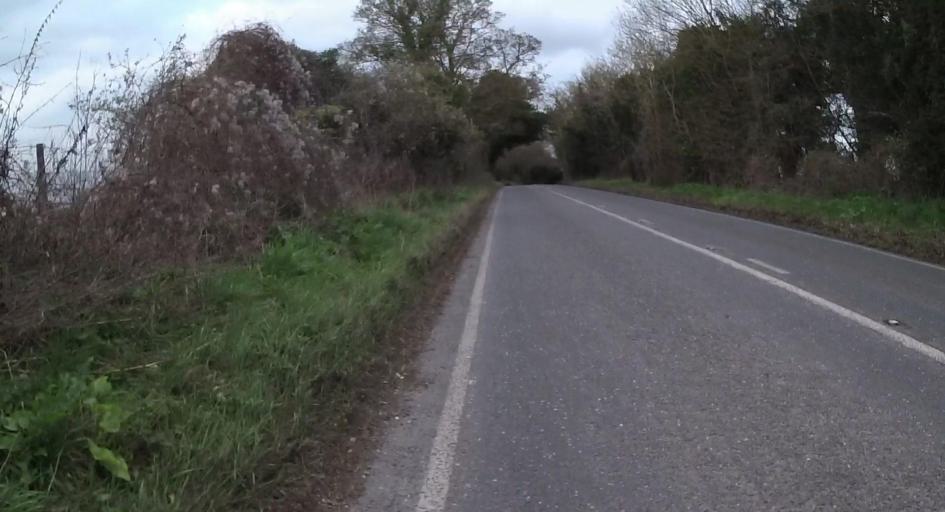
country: GB
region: England
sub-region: Hampshire
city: Kings Worthy
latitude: 51.1722
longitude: -1.3052
